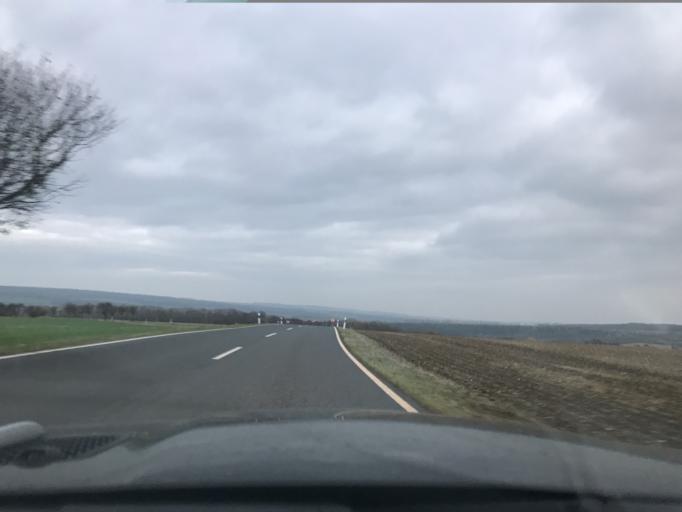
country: DE
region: Thuringia
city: Kullstedt
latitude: 51.2939
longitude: 10.3021
